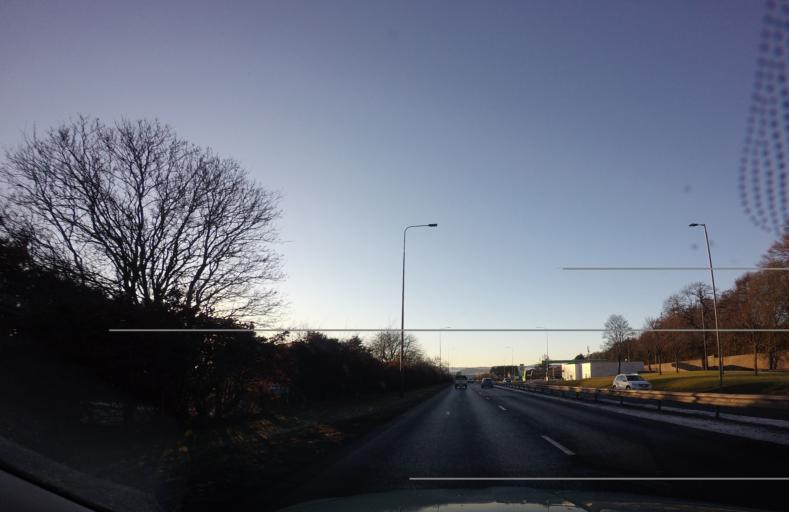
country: GB
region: Scotland
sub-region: Angus
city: Muirhead
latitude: 56.4775
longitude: -3.0324
